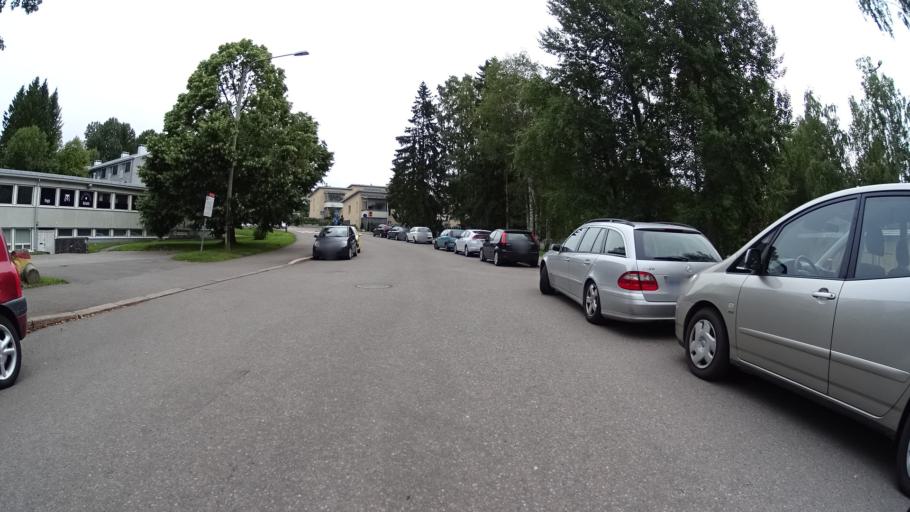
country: FI
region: Uusimaa
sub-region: Helsinki
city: Helsinki
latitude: 60.2293
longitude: 24.8962
